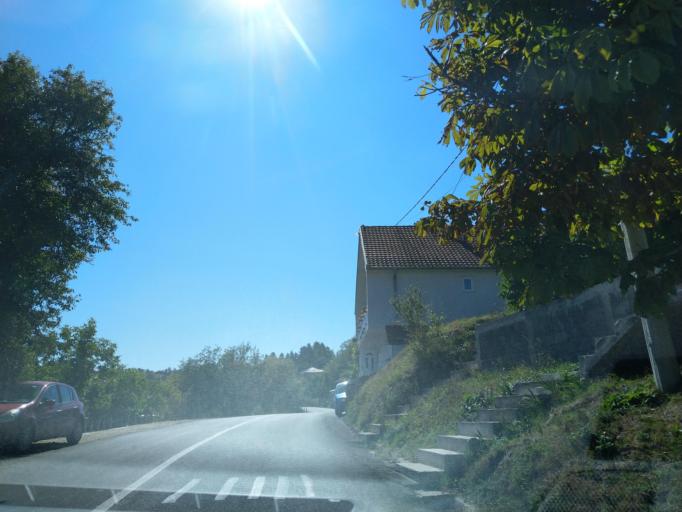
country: RS
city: Sokolovica
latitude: 43.2530
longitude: 20.2287
